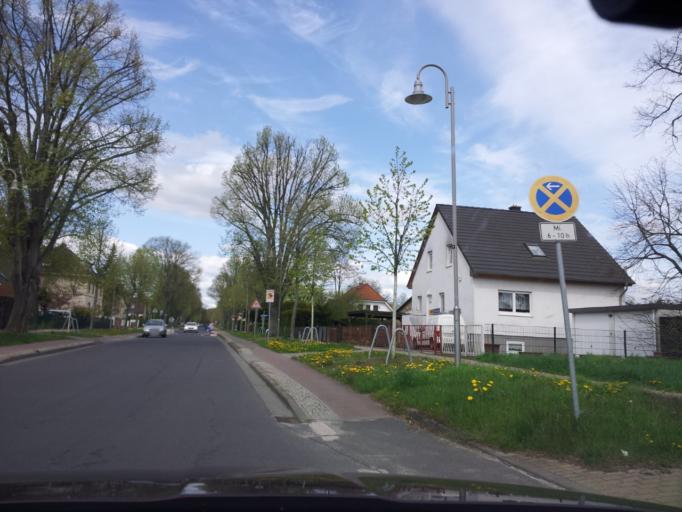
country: DE
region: Brandenburg
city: Teltow
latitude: 52.3898
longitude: 13.2825
